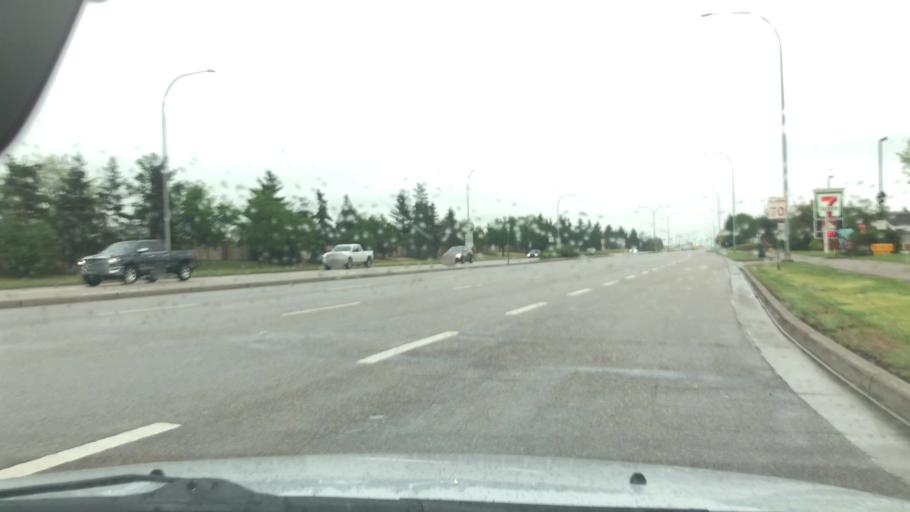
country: CA
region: Alberta
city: Sherwood Park
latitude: 53.5411
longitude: -113.2628
